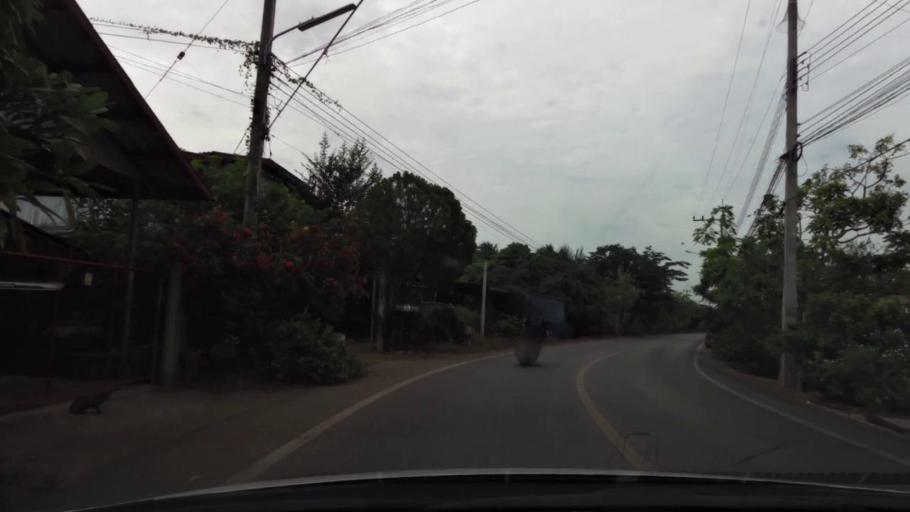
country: TH
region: Ratchaburi
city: Damnoen Saduak
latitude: 13.5720
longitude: 100.0058
